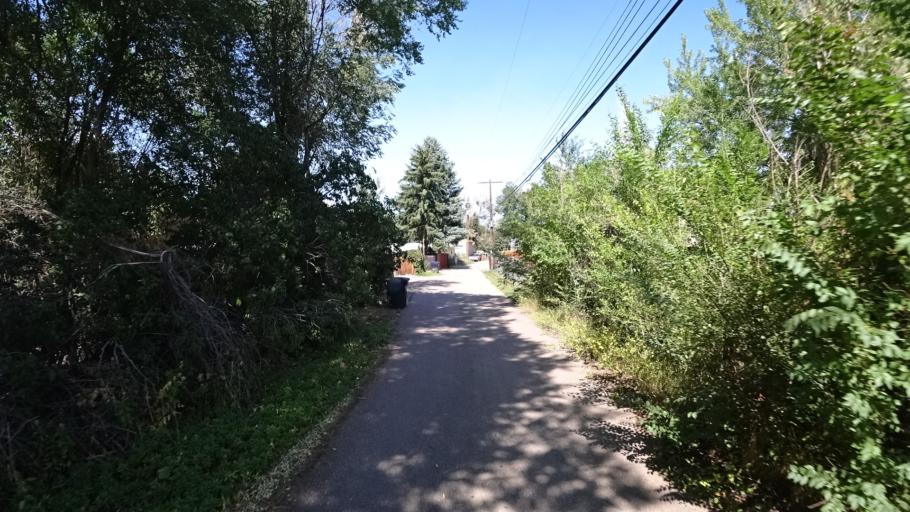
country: US
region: Colorado
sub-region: El Paso County
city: Colorado Springs
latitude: 38.8792
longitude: -104.8061
